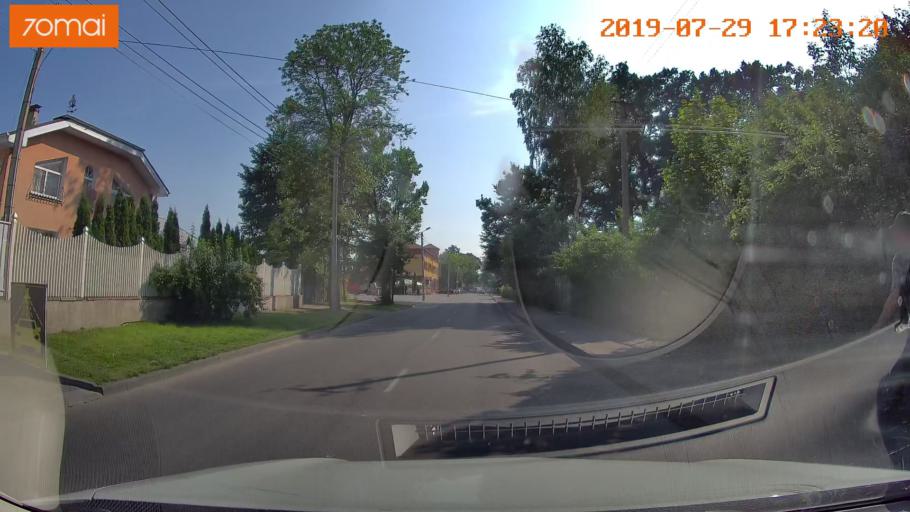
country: RU
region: Kaliningrad
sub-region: Gorod Kaliningrad
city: Kaliningrad
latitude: 54.7666
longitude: 20.4459
